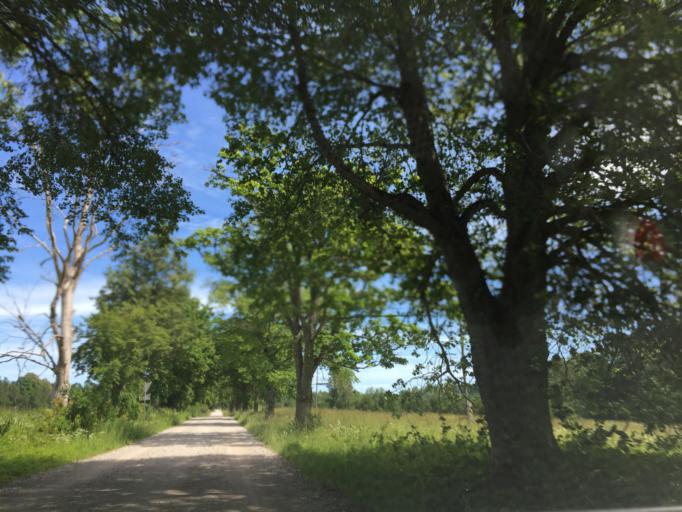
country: LV
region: Dundaga
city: Dundaga
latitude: 57.6193
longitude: 22.2886
